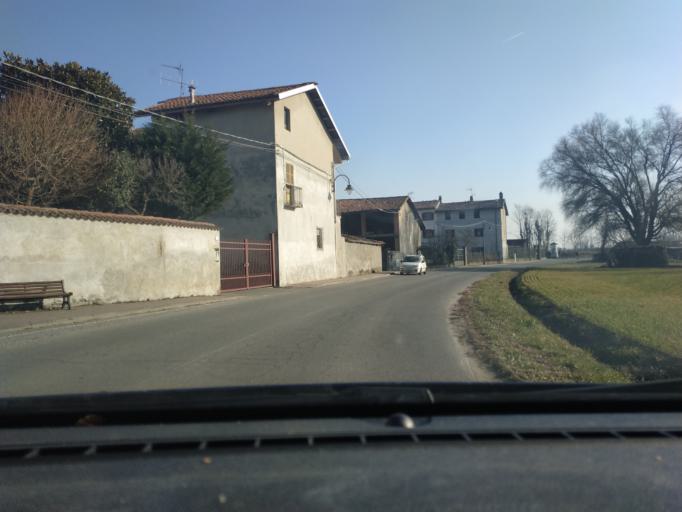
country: IT
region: Piedmont
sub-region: Provincia di Torino
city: Pavone Canavese
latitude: 45.4280
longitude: 7.8614
